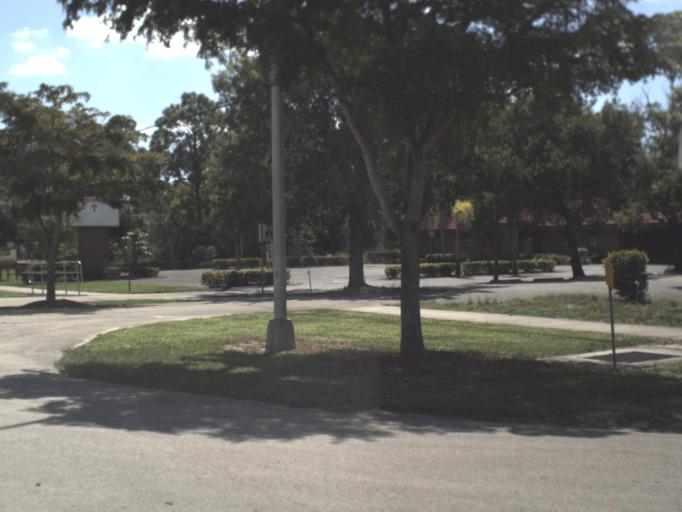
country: US
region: Florida
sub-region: Collier County
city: Lely
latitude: 26.1133
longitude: -81.7537
